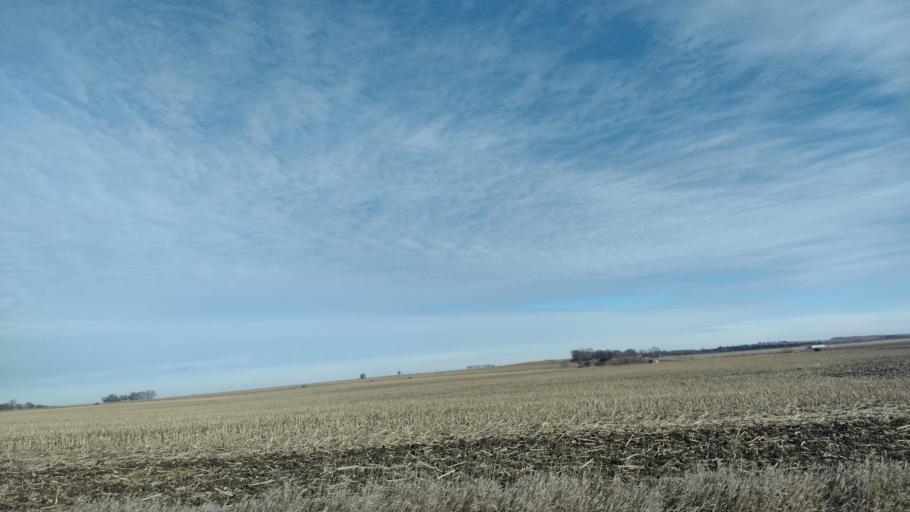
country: US
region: South Dakota
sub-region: Union County
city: Beresford
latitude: 42.9407
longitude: -96.8055
